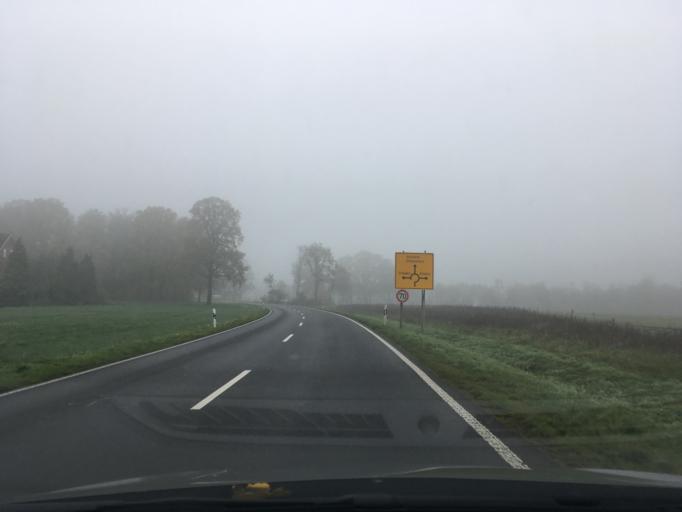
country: DE
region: North Rhine-Westphalia
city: Stadtlohn
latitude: 52.0615
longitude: 6.9365
